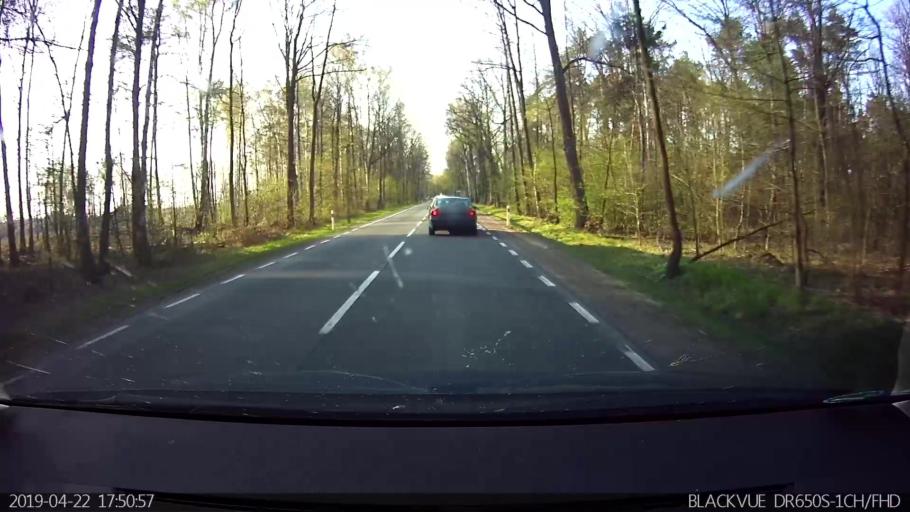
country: PL
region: Masovian Voivodeship
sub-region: Powiat wegrowski
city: Wegrow
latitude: 52.4308
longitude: 21.9978
